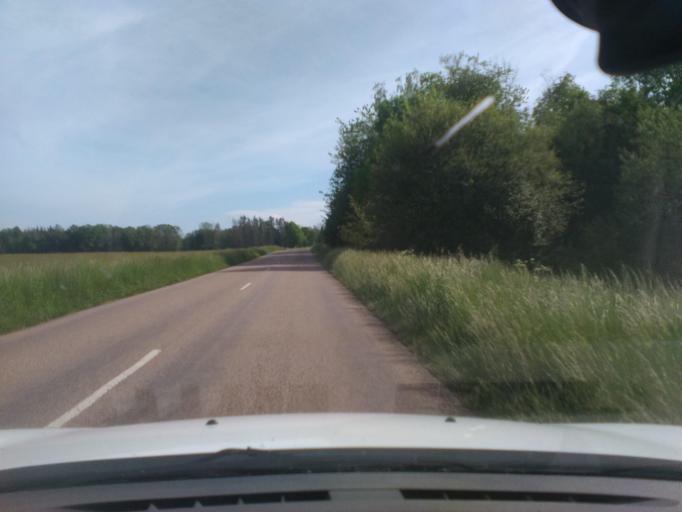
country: FR
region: Lorraine
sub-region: Departement de Meurthe-et-Moselle
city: Gerbeviller
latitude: 48.4287
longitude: 6.5797
